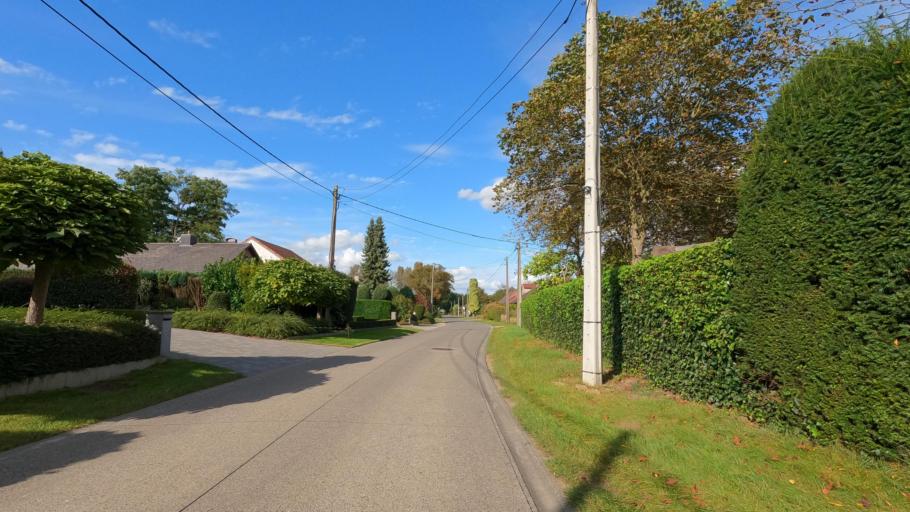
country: BE
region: Flanders
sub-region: Provincie Antwerpen
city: Herselt
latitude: 51.0209
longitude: 4.9157
